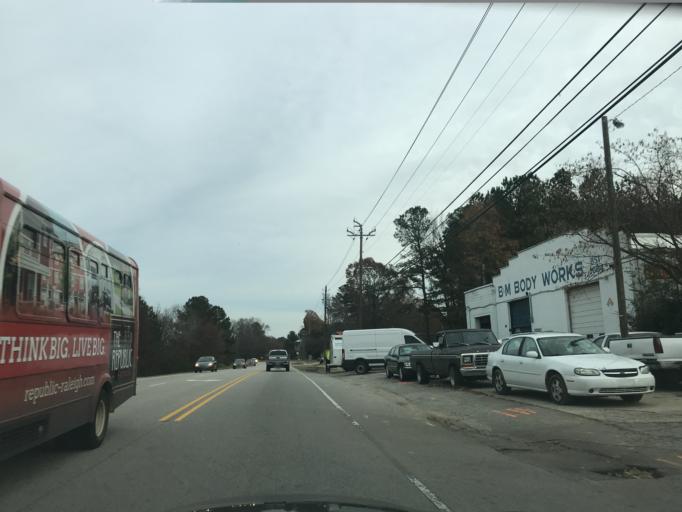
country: US
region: North Carolina
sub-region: Wake County
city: Cary
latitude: 35.7862
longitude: -78.7287
